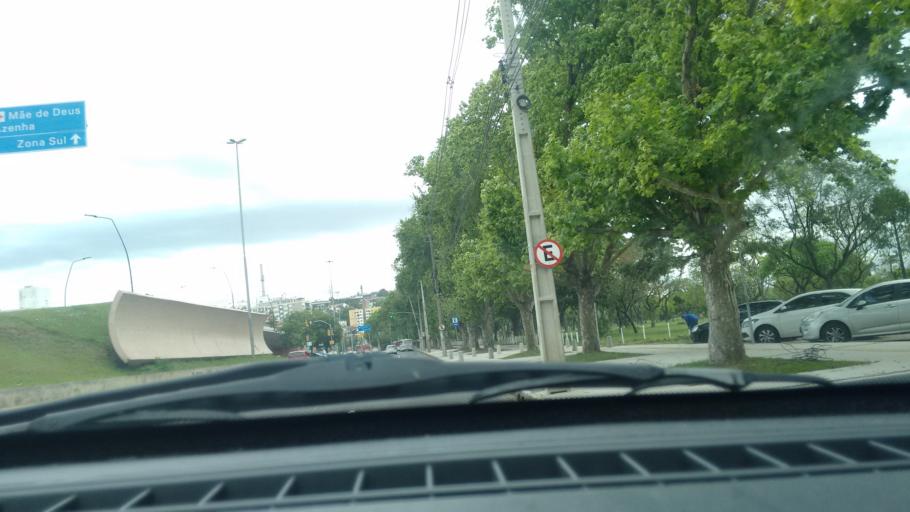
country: BR
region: Rio Grande do Sul
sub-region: Porto Alegre
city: Porto Alegre
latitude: -30.0577
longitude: -51.2307
